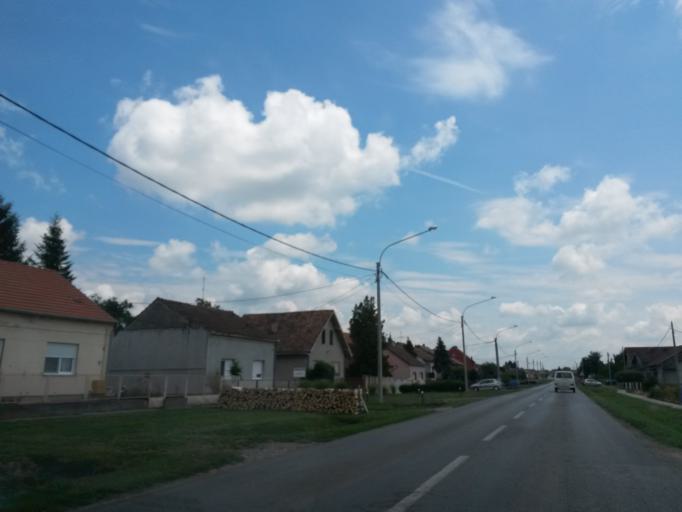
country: HR
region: Osjecko-Baranjska
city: Sarvas
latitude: 45.5289
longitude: 18.8303
